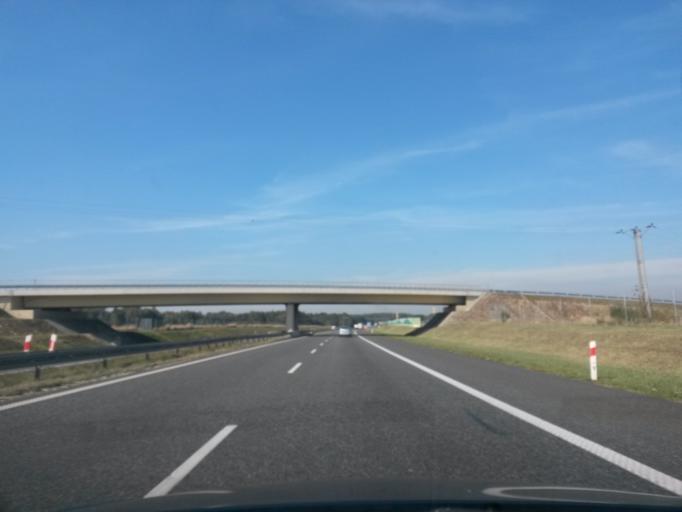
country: PL
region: Silesian Voivodeship
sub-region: Powiat gliwicki
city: Sosnicowice
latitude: 50.2987
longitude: 18.5566
